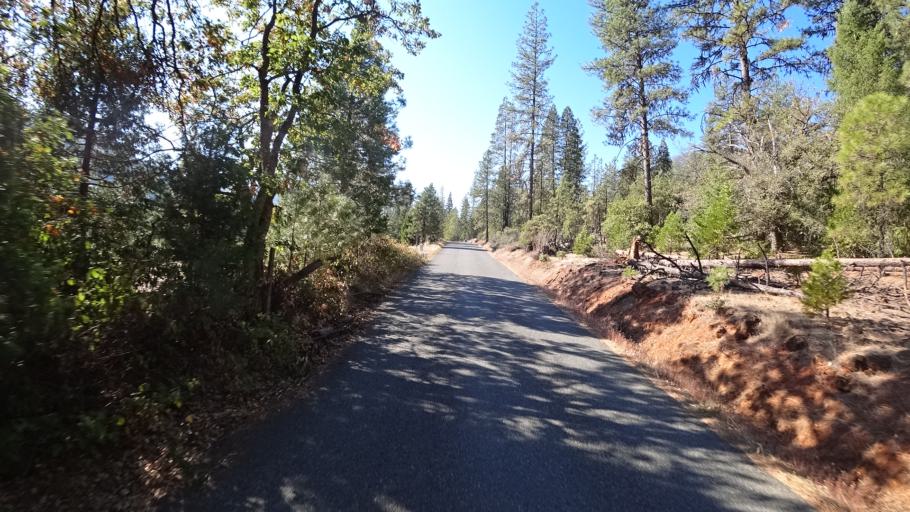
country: US
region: California
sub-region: Siskiyou County
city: Yreka
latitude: 41.7363
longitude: -123.0054
